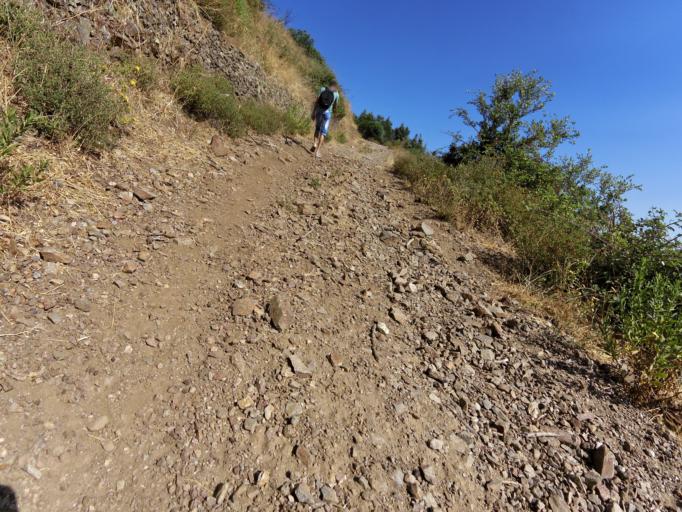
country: IT
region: Calabria
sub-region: Provincia di Reggio Calabria
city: Bivongi
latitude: 38.5003
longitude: 16.4510
